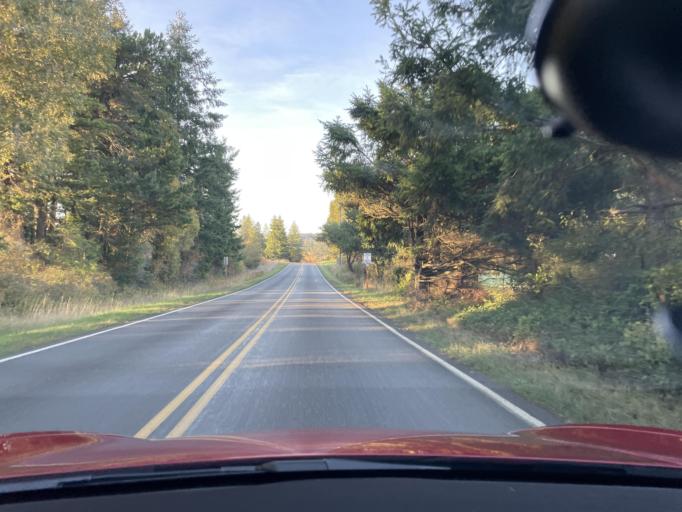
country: US
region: Washington
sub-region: San Juan County
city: Friday Harbor
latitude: 48.5625
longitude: -123.1410
